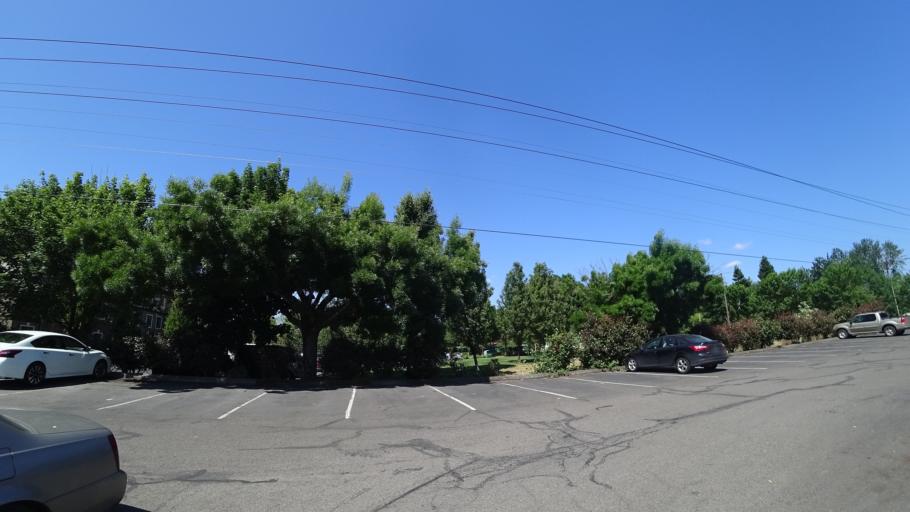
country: US
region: Washington
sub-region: Clark County
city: Mill Plain
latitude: 45.5680
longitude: -122.5401
